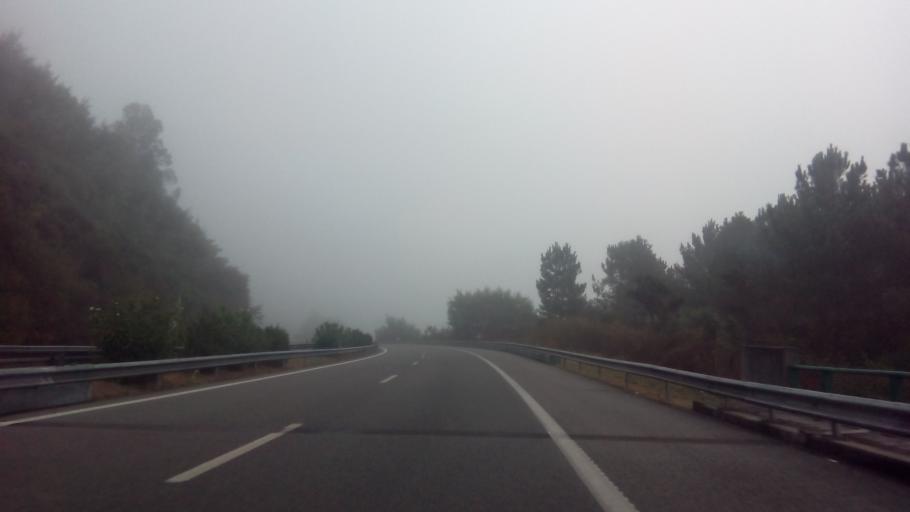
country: PT
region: Porto
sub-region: Marco de Canaveses
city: Marco de Canavezes
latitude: 41.2283
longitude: -8.1300
